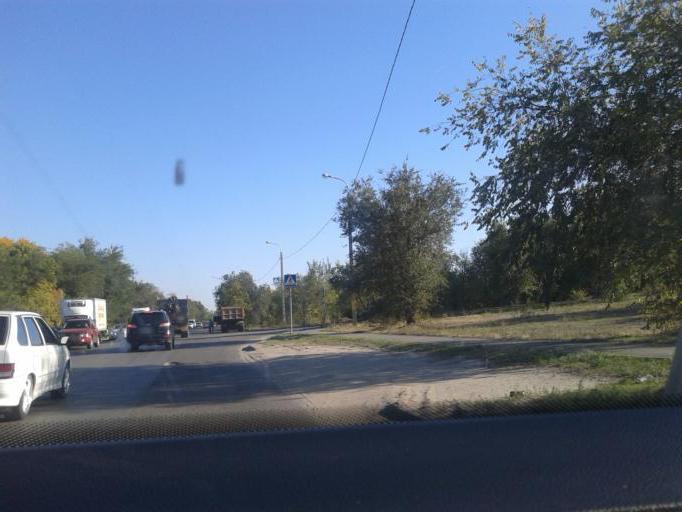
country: RU
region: Volgograd
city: Volgograd
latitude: 48.7622
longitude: 44.5196
